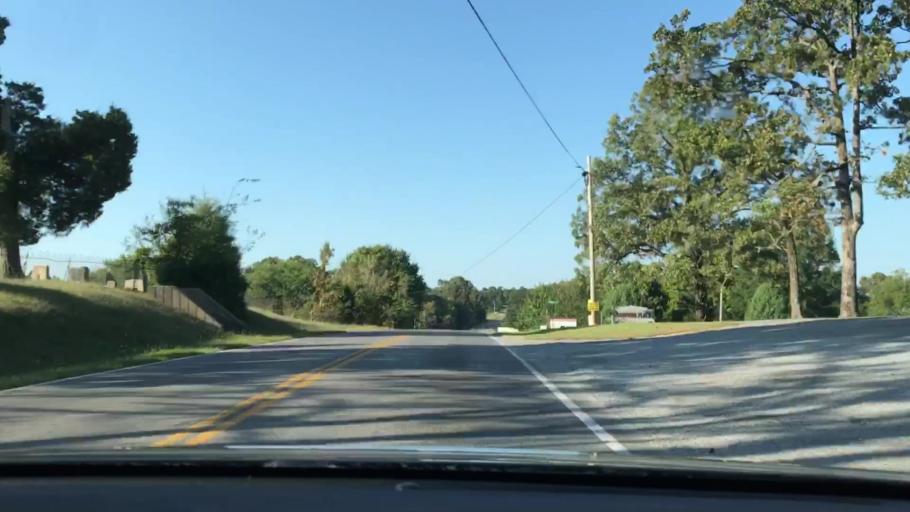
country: US
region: Kentucky
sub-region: Trigg County
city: Cadiz
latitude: 36.8156
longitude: -87.8795
